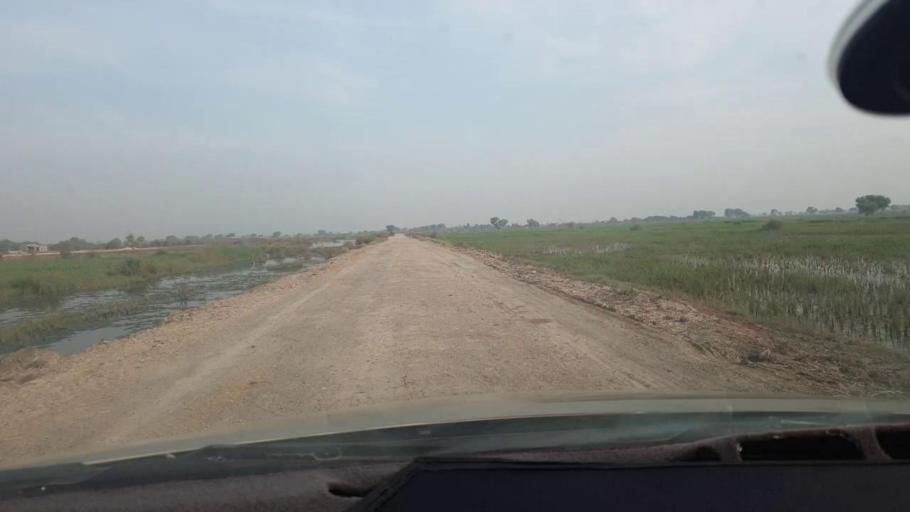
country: PK
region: Balochistan
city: Jhatpat
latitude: 28.3607
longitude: 68.4070
